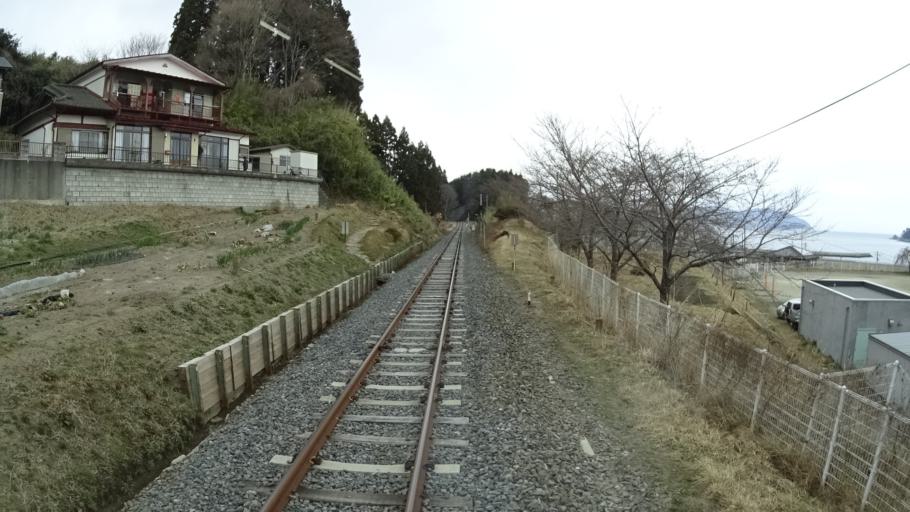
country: JP
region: Iwate
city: Otsuchi
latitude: 39.3721
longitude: 141.9401
